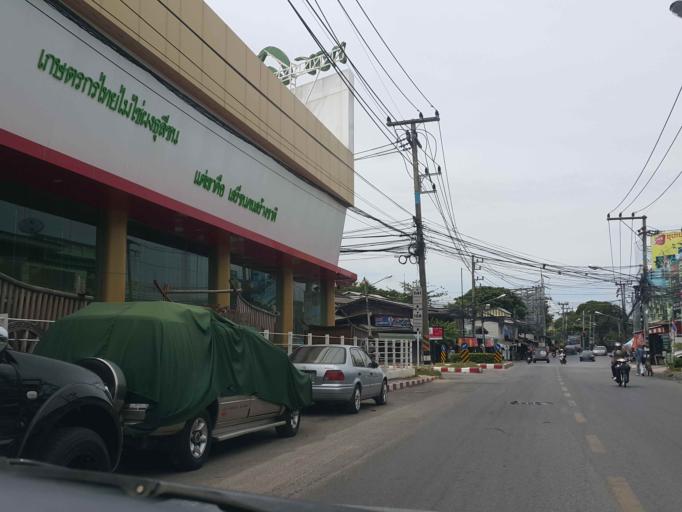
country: TH
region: Chiang Mai
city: Chiang Mai
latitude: 18.7754
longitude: 98.9809
